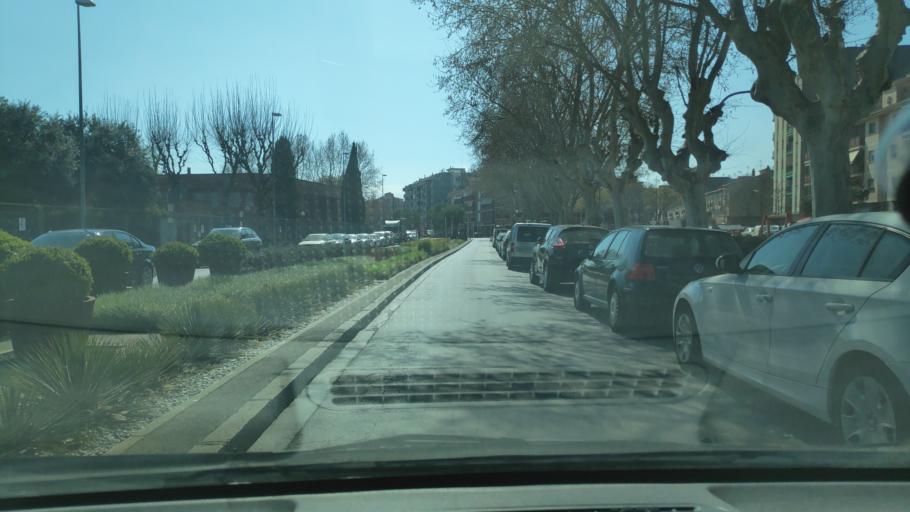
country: ES
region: Catalonia
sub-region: Provincia de Barcelona
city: Mollet del Valles
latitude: 41.5439
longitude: 2.2202
